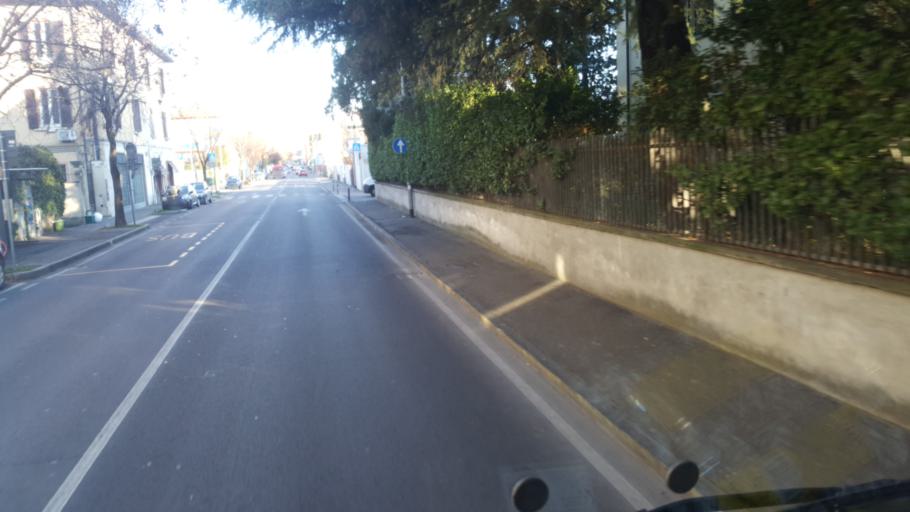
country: IT
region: Lombardy
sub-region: Provincia di Bergamo
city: Bergamo
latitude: 45.6811
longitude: 9.6620
